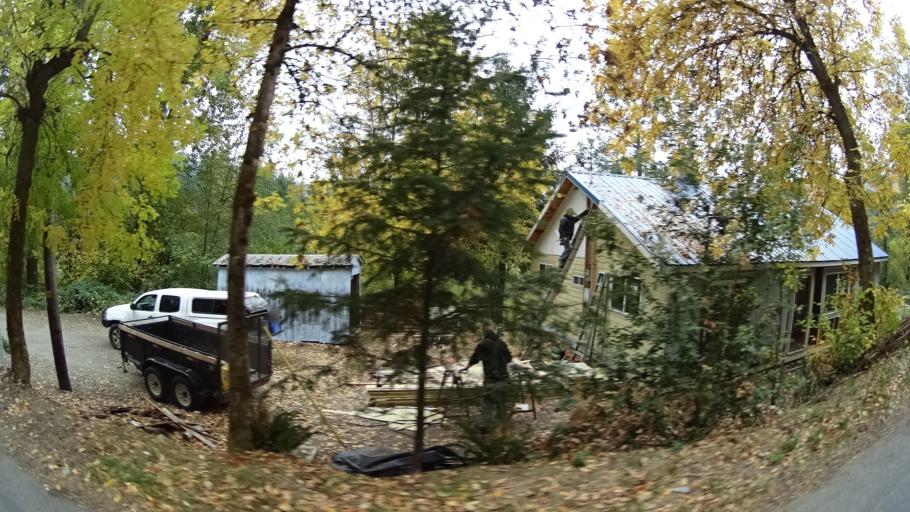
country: US
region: California
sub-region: Siskiyou County
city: Happy Camp
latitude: 41.7910
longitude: -123.3706
